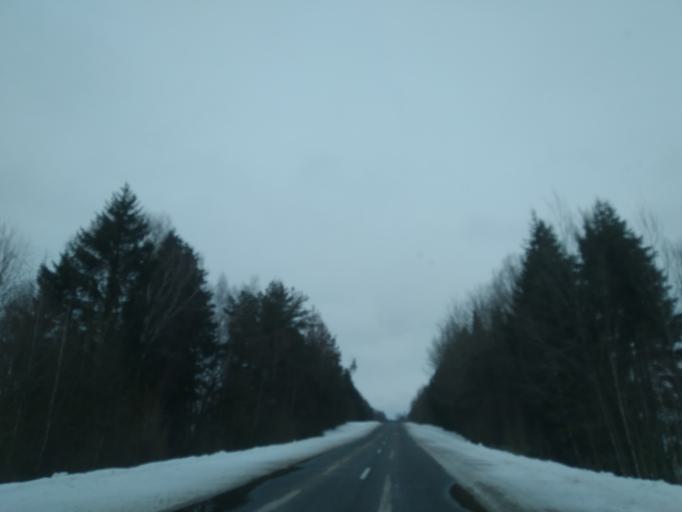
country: BY
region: Minsk
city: Ivyanyets
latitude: 53.8526
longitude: 26.7879
